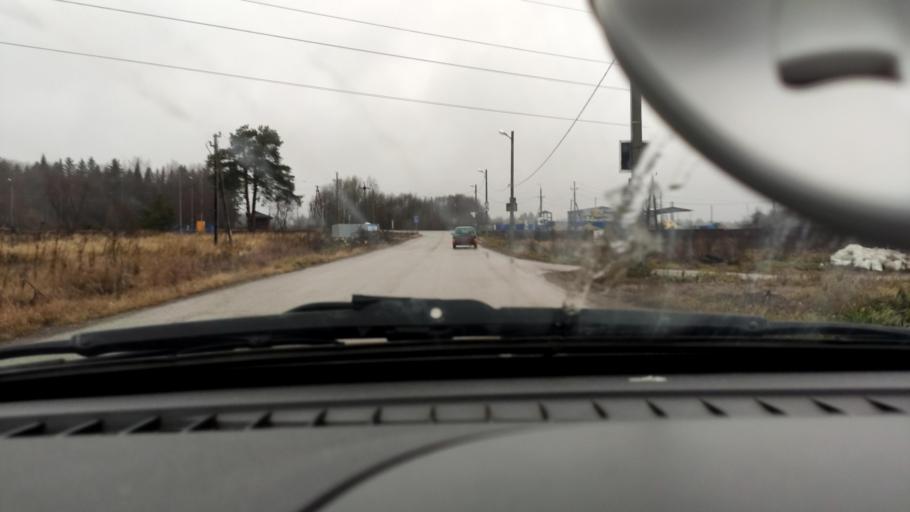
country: RU
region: Perm
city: Perm
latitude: 58.0410
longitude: 56.4081
